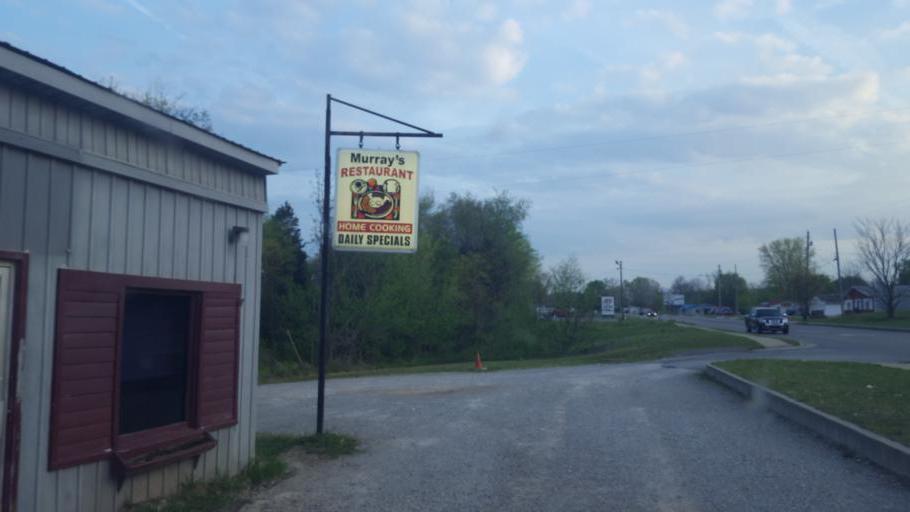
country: US
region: Kentucky
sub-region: Hart County
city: Munfordville
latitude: 37.2806
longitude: -85.8986
